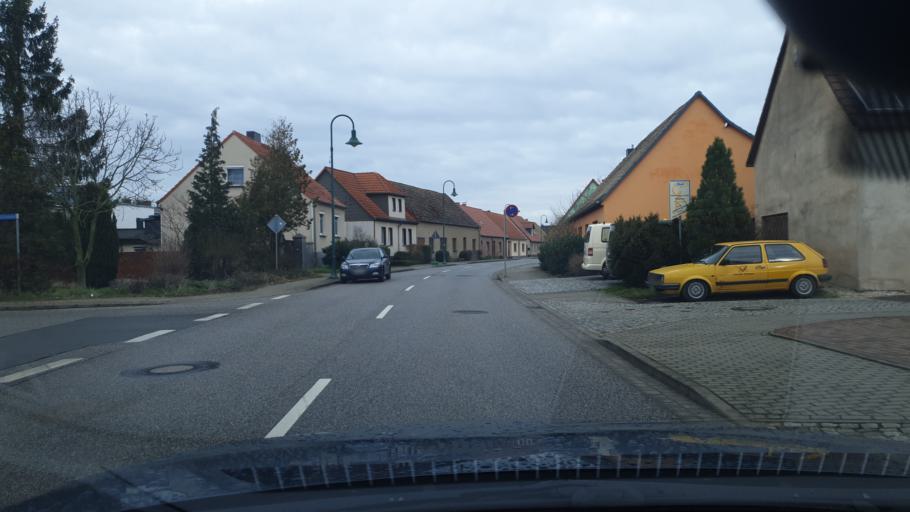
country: DE
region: Saxony-Anhalt
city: Vockerode
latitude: 51.8453
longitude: 12.3532
